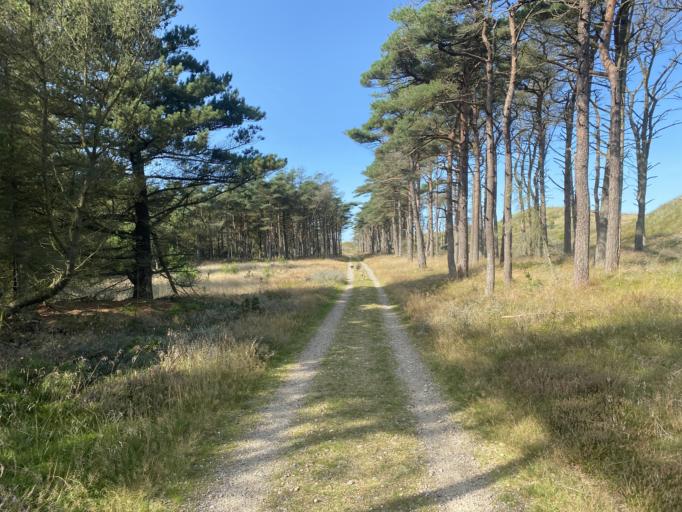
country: DK
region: Central Jutland
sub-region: Holstebro Kommune
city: Ulfborg
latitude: 56.2919
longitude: 8.1445
